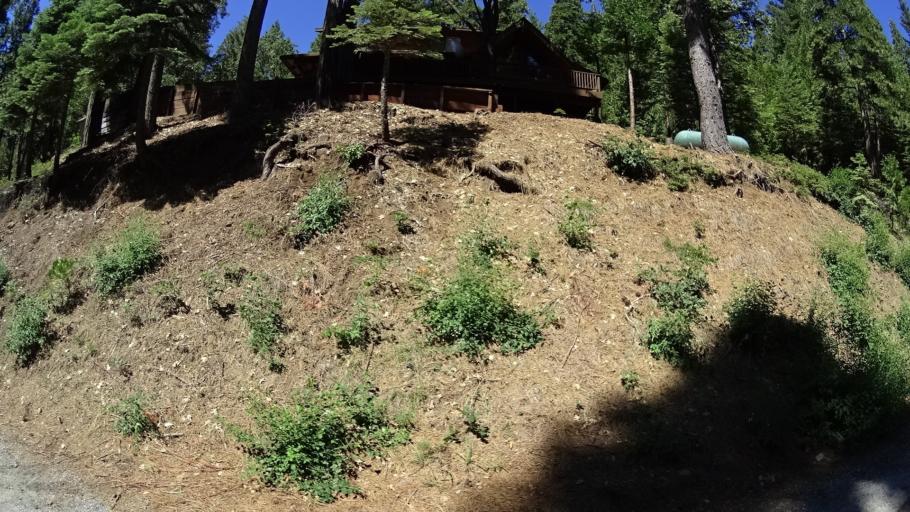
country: US
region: California
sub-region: Calaveras County
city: Arnold
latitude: 38.2889
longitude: -120.2863
